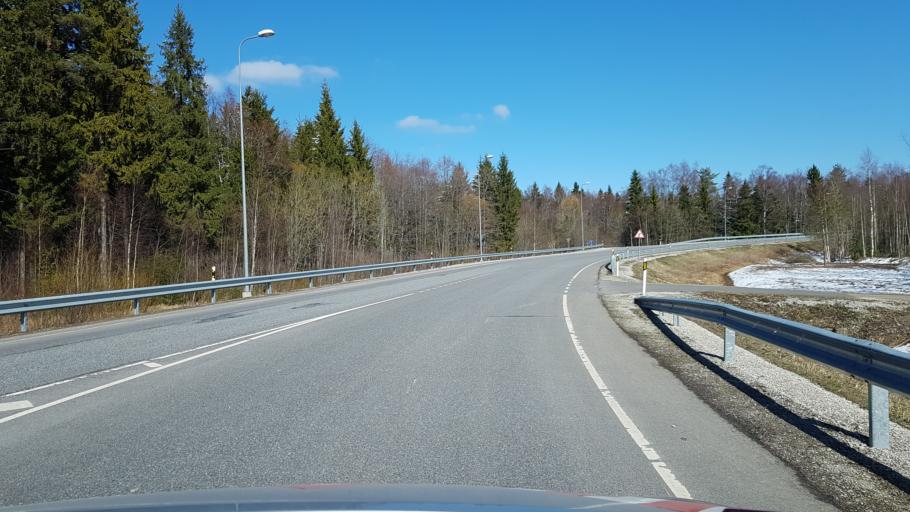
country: EE
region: Laeaene-Virumaa
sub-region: Tapa vald
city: Tapa
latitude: 59.4552
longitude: 25.9376
